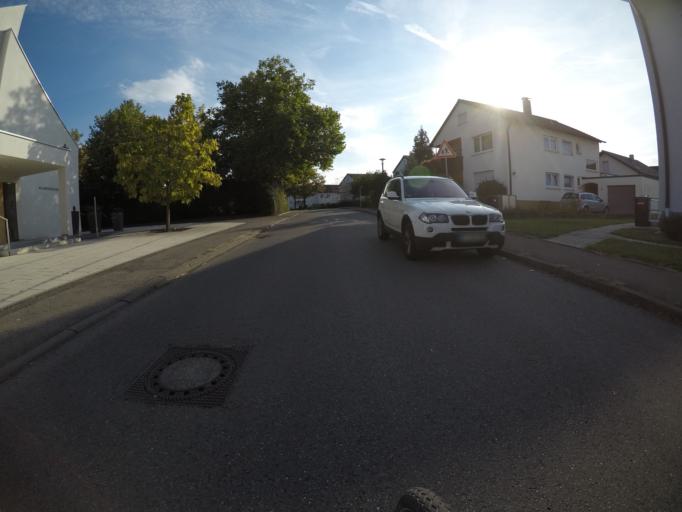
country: DE
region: Baden-Wuerttemberg
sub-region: Tuebingen Region
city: Sickenhausen
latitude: 48.5300
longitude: 9.1983
